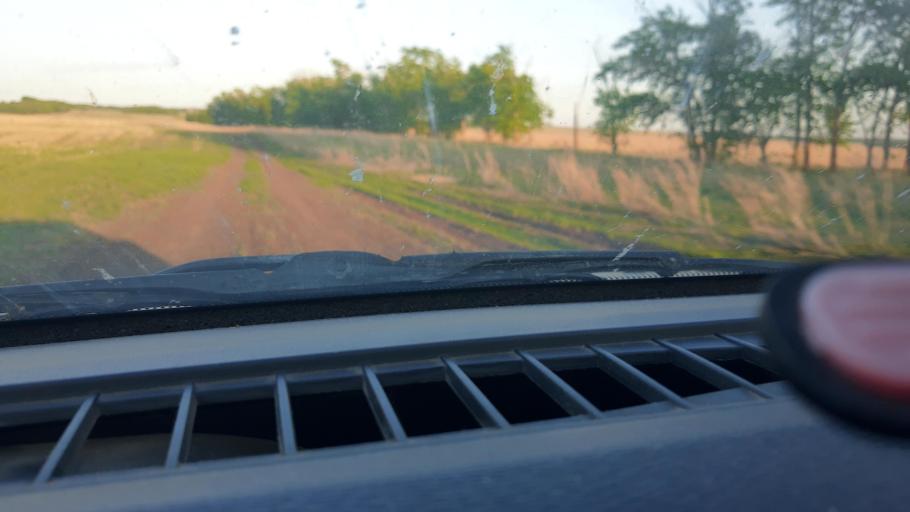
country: RU
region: Bashkortostan
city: Asanovo
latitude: 54.8824
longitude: 55.4975
